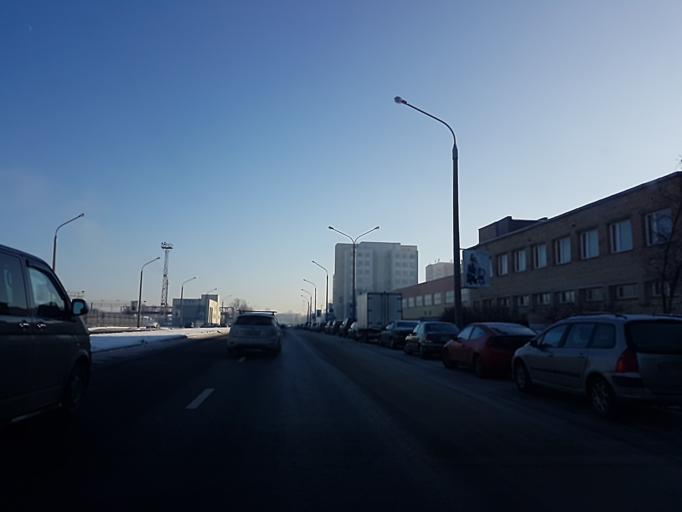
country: BY
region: Minsk
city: Minsk
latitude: 53.9011
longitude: 27.5271
